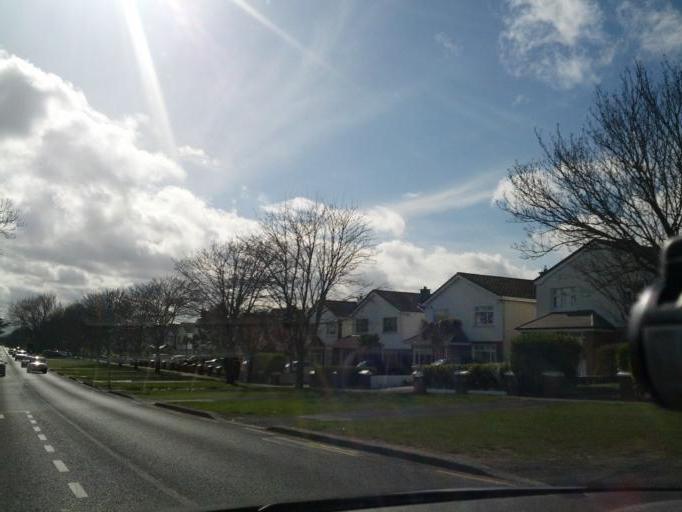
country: IE
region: Leinster
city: Portmarnock
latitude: 53.4276
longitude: -6.1294
